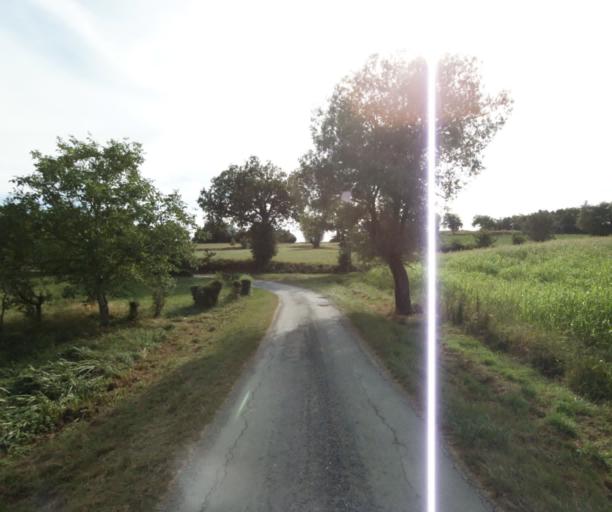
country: FR
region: Midi-Pyrenees
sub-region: Departement du Tarn
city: Puylaurens
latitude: 43.5350
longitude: 2.0585
